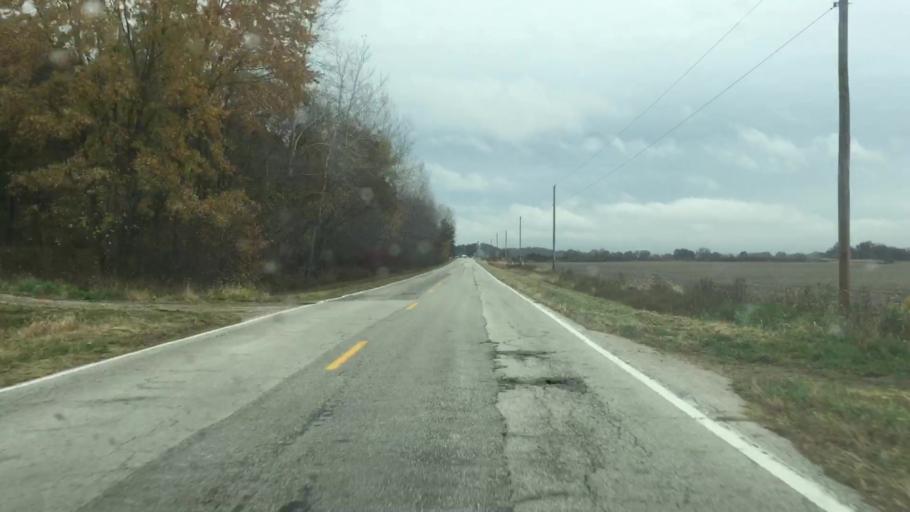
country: US
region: Missouri
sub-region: Gasconade County
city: Hermann
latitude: 38.7101
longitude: -91.5394
